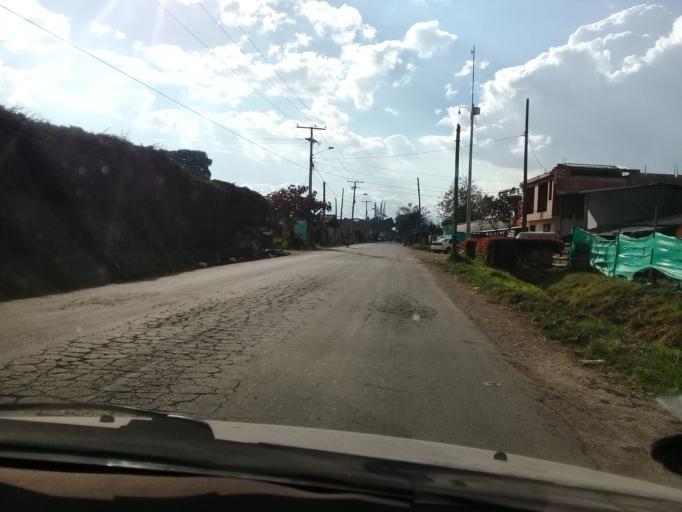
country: CO
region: Cundinamarca
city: El Rosal
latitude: 4.8168
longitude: -74.2470
